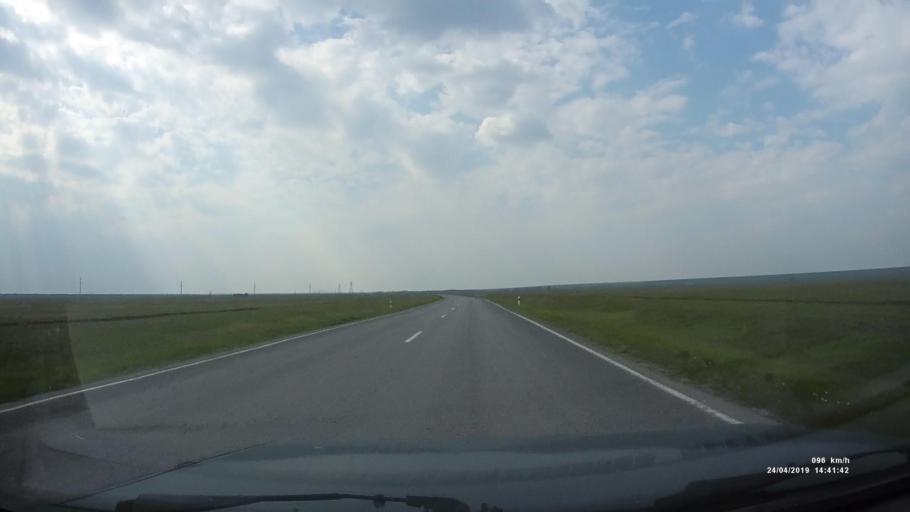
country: RU
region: Rostov
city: Remontnoye
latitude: 46.4472
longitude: 43.8758
